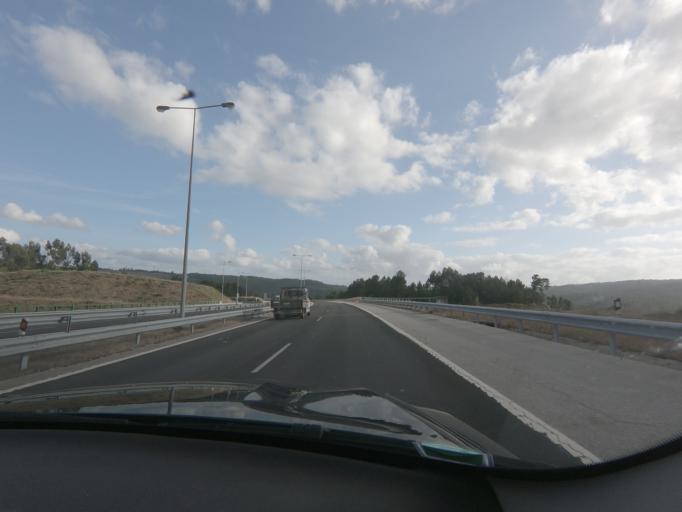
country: PT
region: Viseu
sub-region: Castro Daire
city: Castro Daire
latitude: 40.8590
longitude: -7.9291
